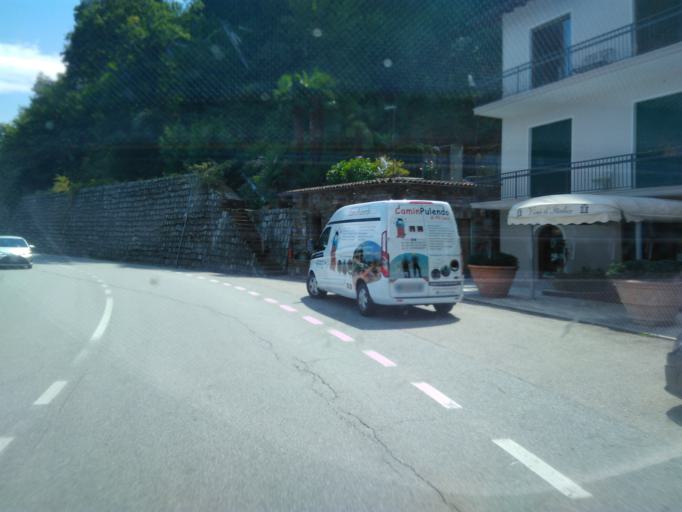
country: CH
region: Ticino
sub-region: Locarno District
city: Brissago
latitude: 46.0987
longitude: 8.6933
